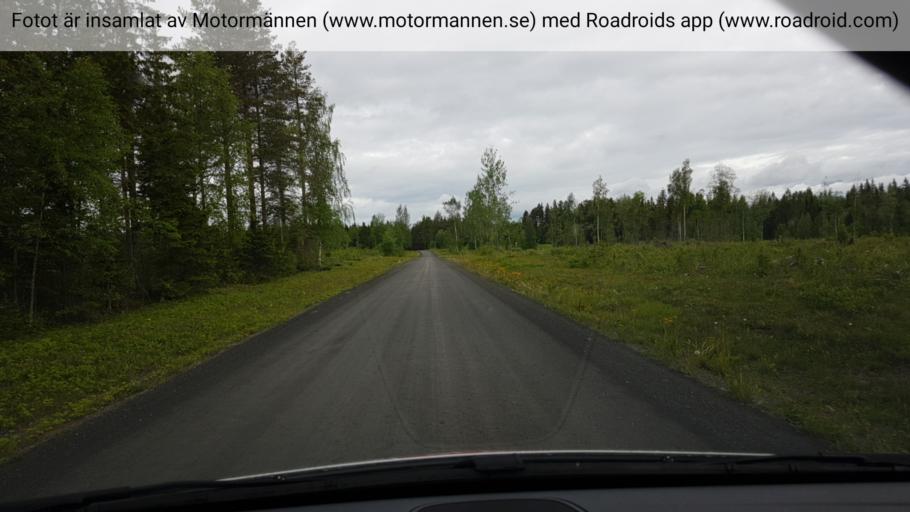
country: SE
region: Jaemtland
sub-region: OEstersunds Kommun
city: Lit
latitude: 63.2394
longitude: 15.0297
